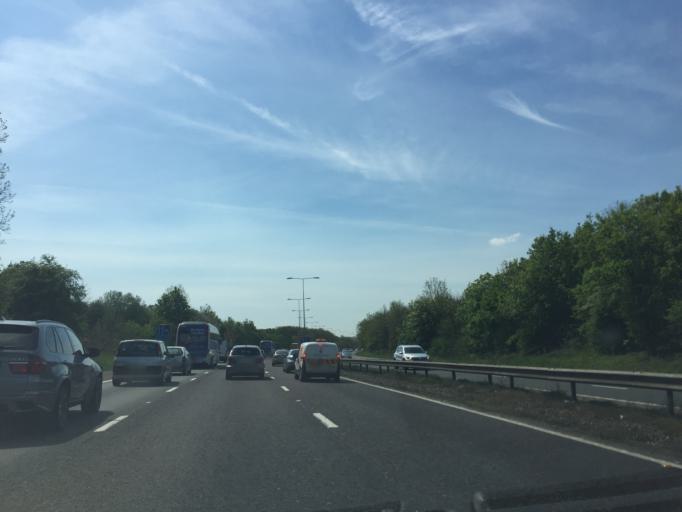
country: GB
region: England
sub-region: Essex
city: Chigwell
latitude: 51.6160
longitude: 0.0604
